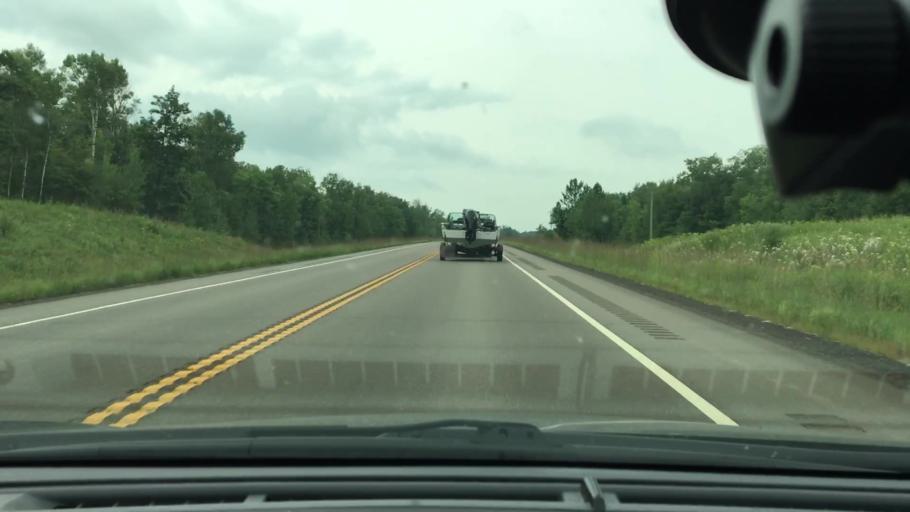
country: US
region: Minnesota
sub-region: Crow Wing County
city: Crosby
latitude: 46.6117
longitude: -93.9488
